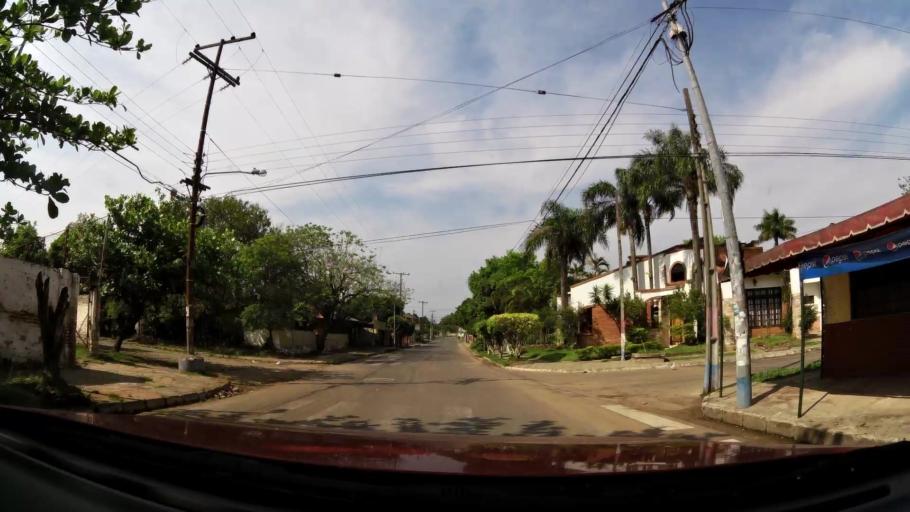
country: PY
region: Central
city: Fernando de la Mora
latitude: -25.2662
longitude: -57.5488
